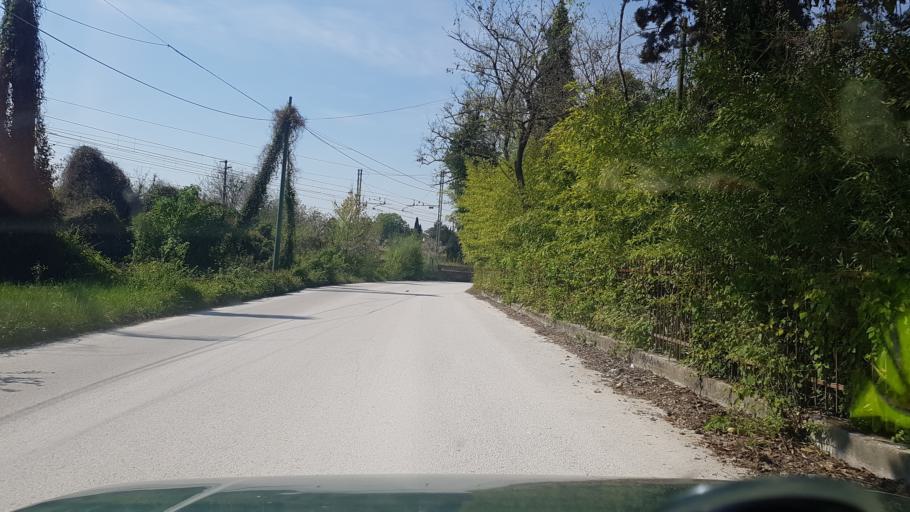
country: IT
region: Friuli Venezia Giulia
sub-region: Provincia di Gorizia
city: Ronchi dei Legionari
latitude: 45.8455
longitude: 13.4916
